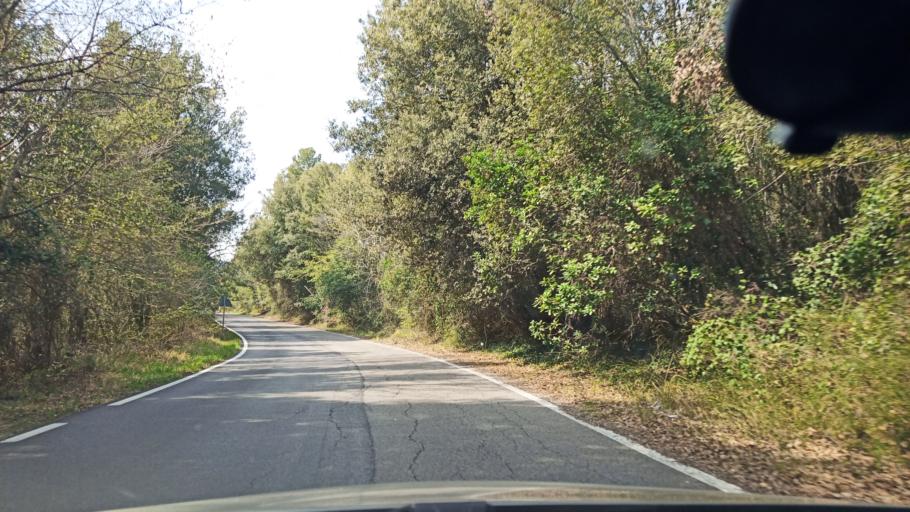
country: IT
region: Latium
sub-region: Provincia di Rieti
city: Vacone
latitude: 42.3643
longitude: 12.6644
